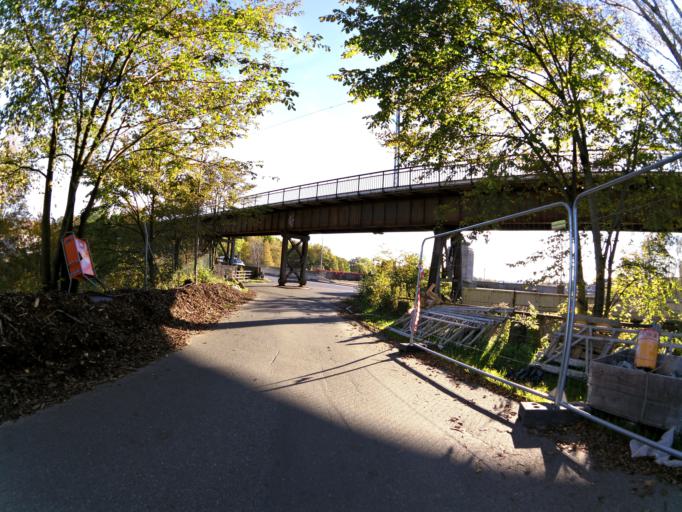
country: NO
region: Ostfold
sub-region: Sarpsborg
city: Sarpsborg
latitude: 59.2775
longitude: 11.1312
